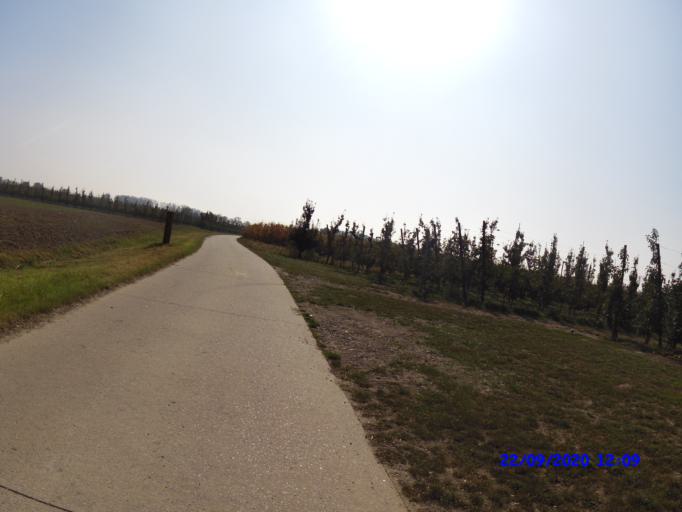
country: BE
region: Flanders
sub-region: Provincie Limburg
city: Alken
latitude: 50.8530
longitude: 5.3032
